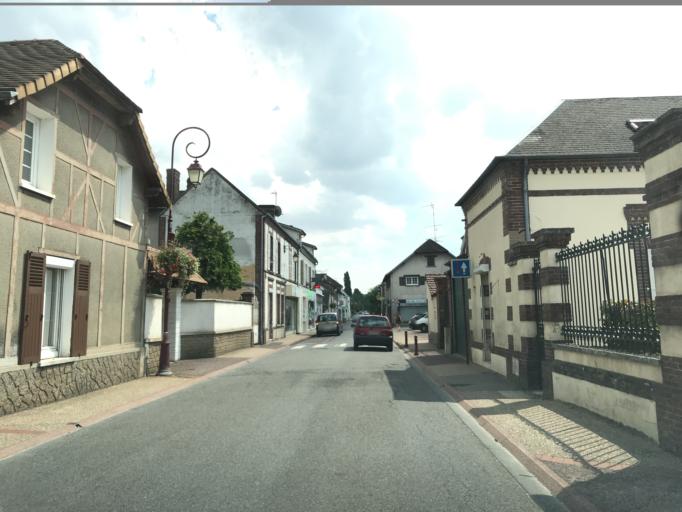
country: FR
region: Haute-Normandie
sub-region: Departement de l'Eure
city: Ezy-sur-Eure
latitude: 48.8649
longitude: 1.4206
